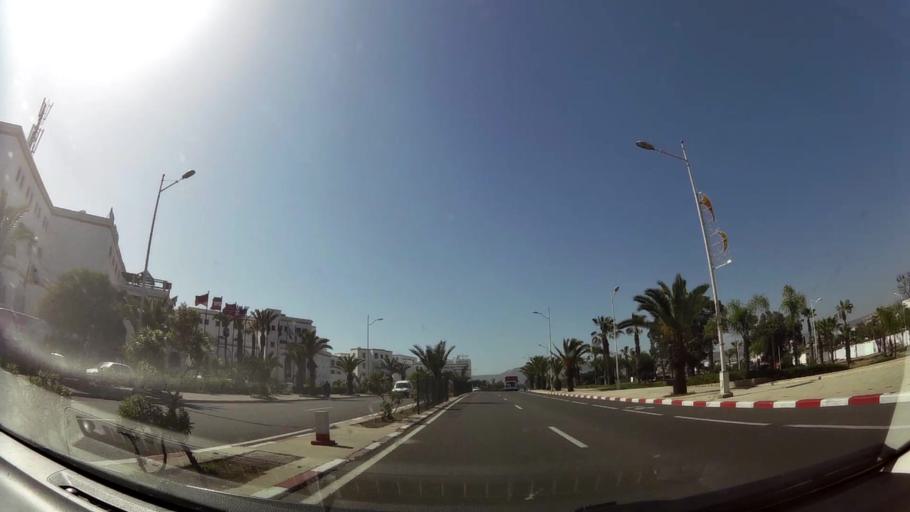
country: MA
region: Souss-Massa-Draa
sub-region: Agadir-Ida-ou-Tnan
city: Agadir
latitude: 30.4137
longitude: -9.5975
